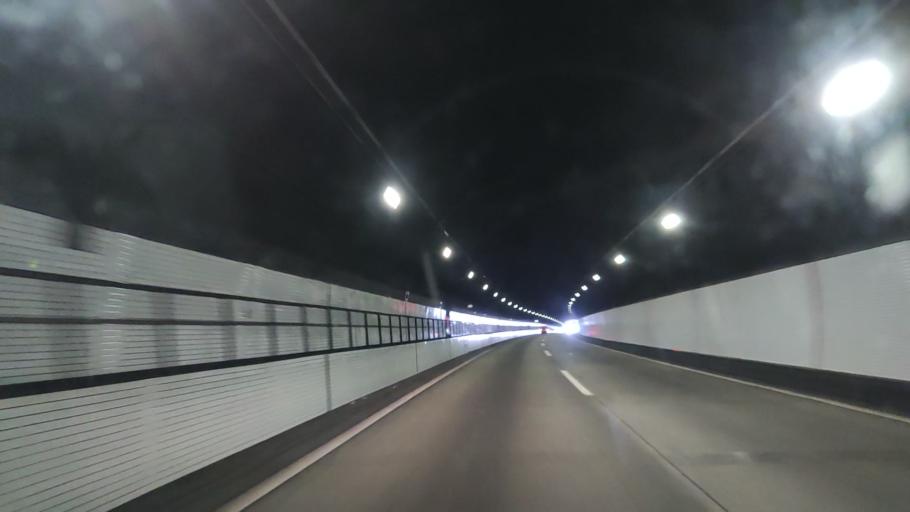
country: JP
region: Ehime
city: Niihama
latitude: 33.9166
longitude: 133.3008
